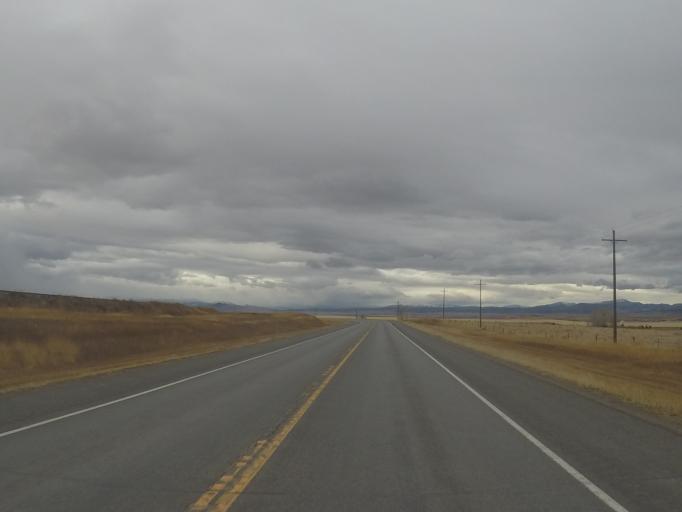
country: US
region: Montana
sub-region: Lewis and Clark County
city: East Helena
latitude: 46.5590
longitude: -111.7777
